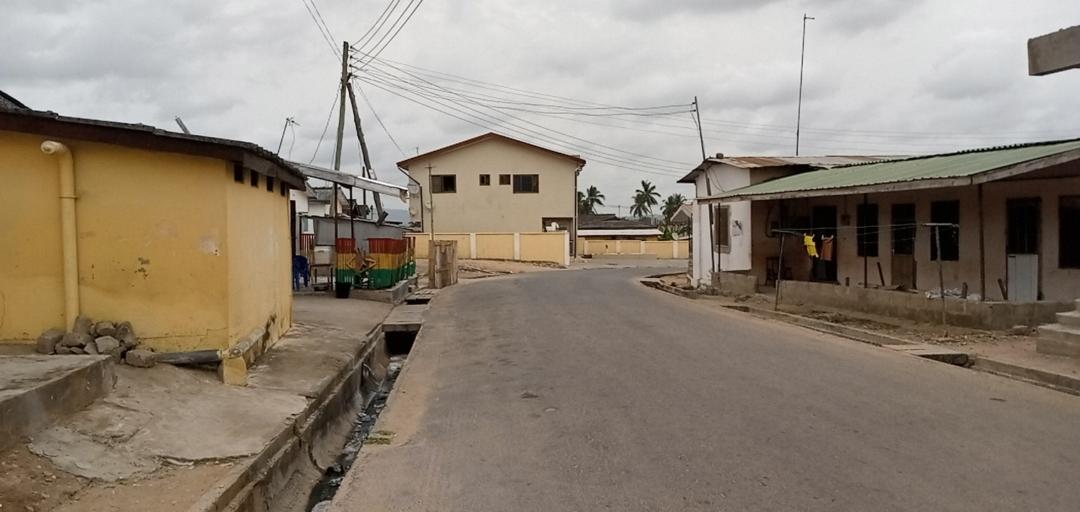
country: GH
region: Central
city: Winneba
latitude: 5.3494
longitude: -0.6221
